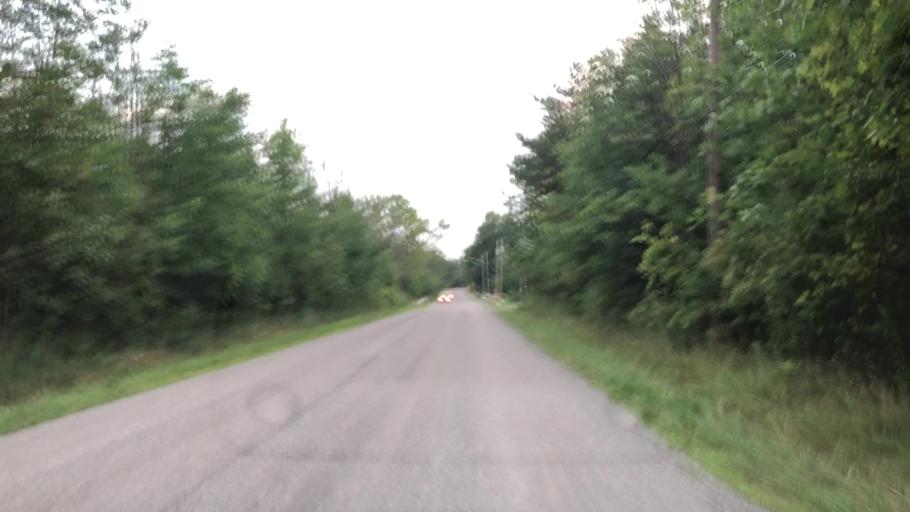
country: US
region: New York
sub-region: Erie County
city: Elma Center
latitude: 42.8395
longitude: -78.6798
